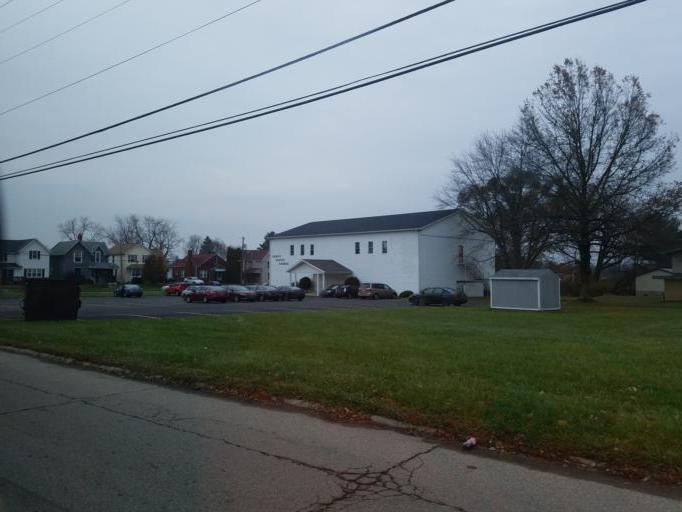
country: US
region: Ohio
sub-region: Richland County
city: Mansfield
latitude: 40.7509
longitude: -82.5076
